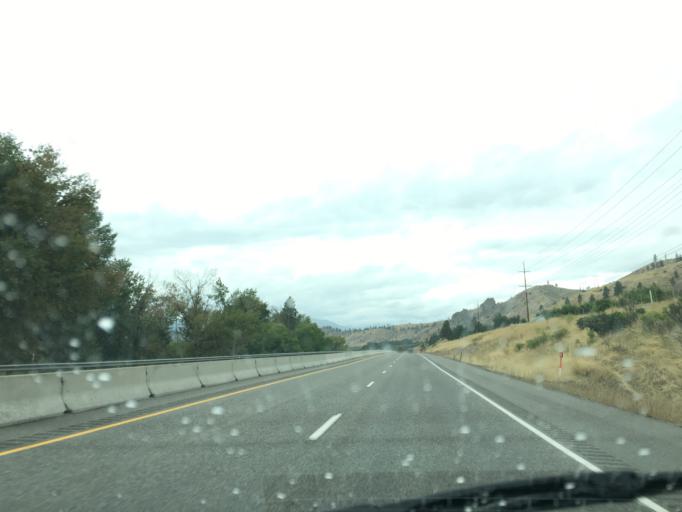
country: US
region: Washington
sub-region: Chelan County
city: Cashmere
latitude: 47.5308
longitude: -120.4987
